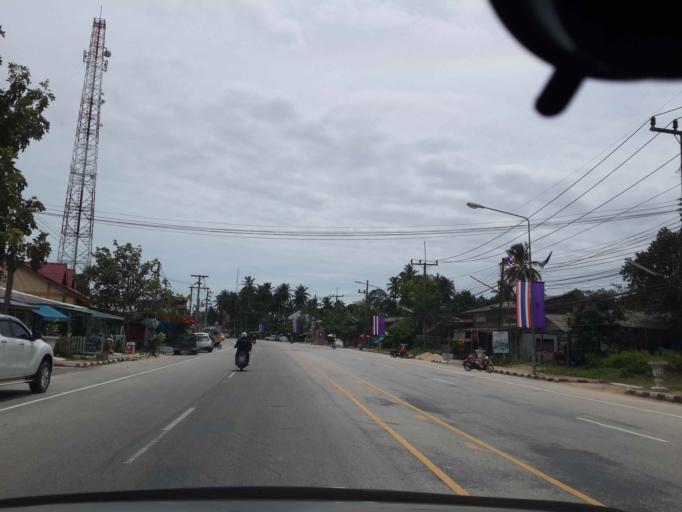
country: TH
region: Narathiwat
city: Yi-ngo
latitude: 6.4031
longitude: 101.7088
